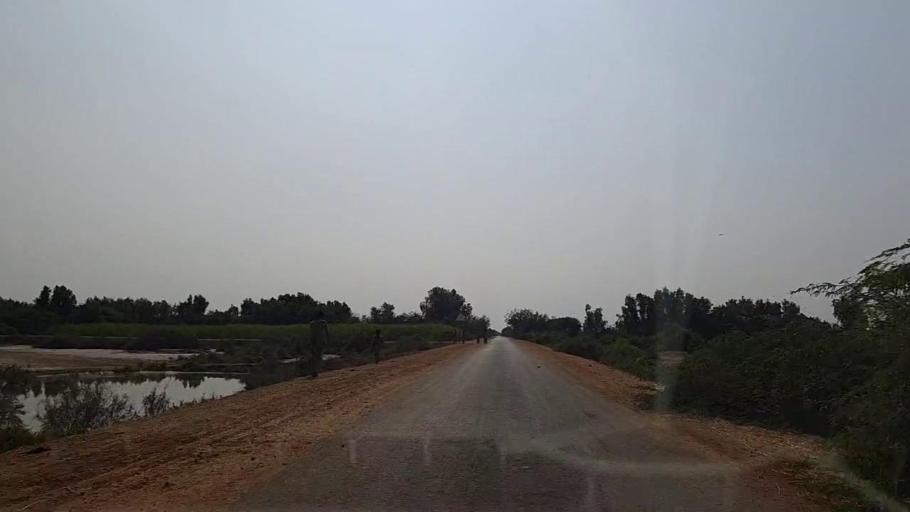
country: PK
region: Sindh
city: Chuhar Jamali
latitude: 24.2630
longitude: 67.9087
